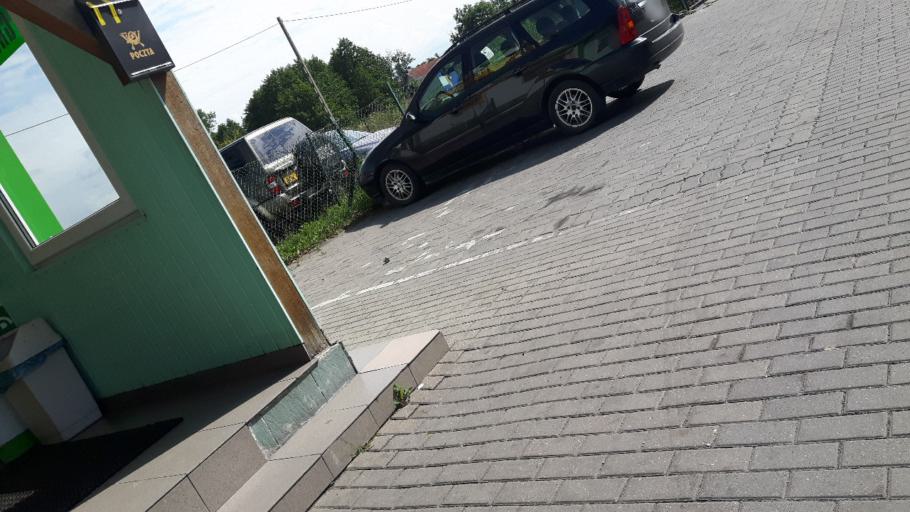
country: RU
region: Kaliningrad
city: Mamonovo
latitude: 54.4306
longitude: 19.8936
